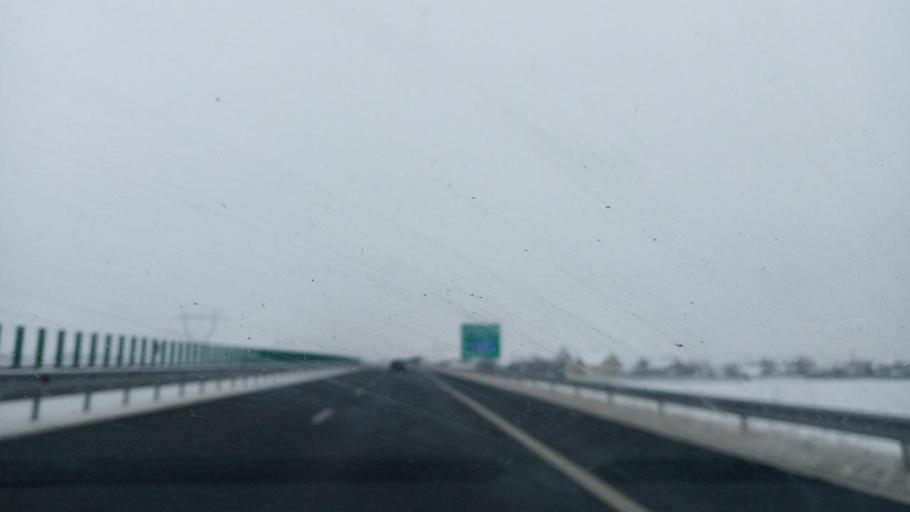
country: RO
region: Bacau
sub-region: Comuna Letea Veche
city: Holt
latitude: 46.5790
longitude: 26.9643
